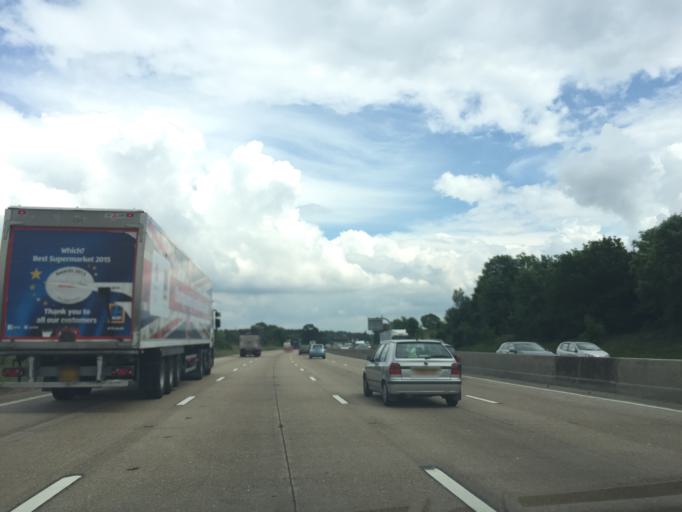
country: GB
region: England
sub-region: Hertfordshire
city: Cuffley
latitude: 51.6887
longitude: -0.1319
